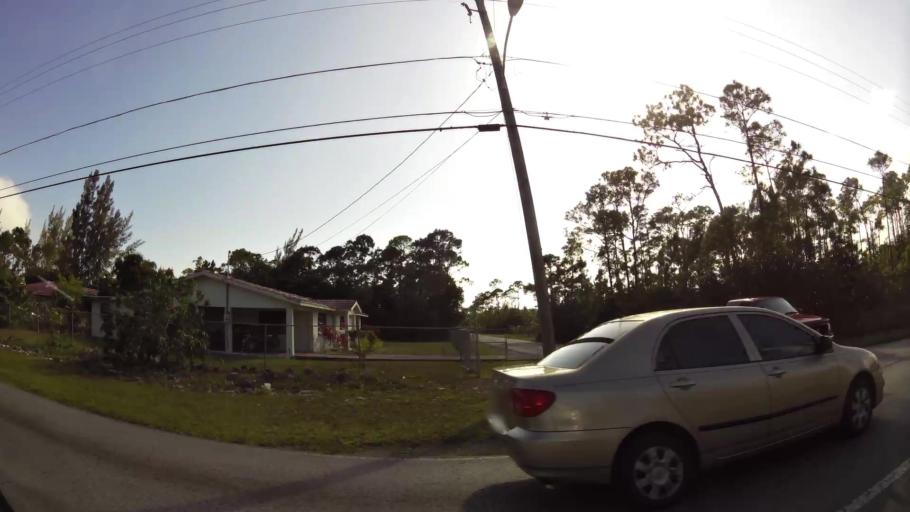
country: BS
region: Freeport
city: Lucaya
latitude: 26.5162
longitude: -78.6662
